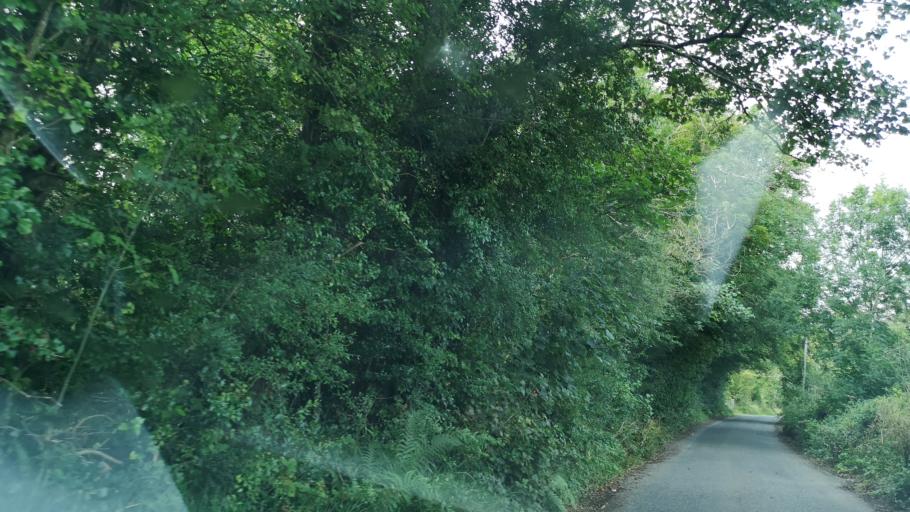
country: IE
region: Connaught
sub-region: County Galway
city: Loughrea
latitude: 53.3011
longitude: -8.6008
